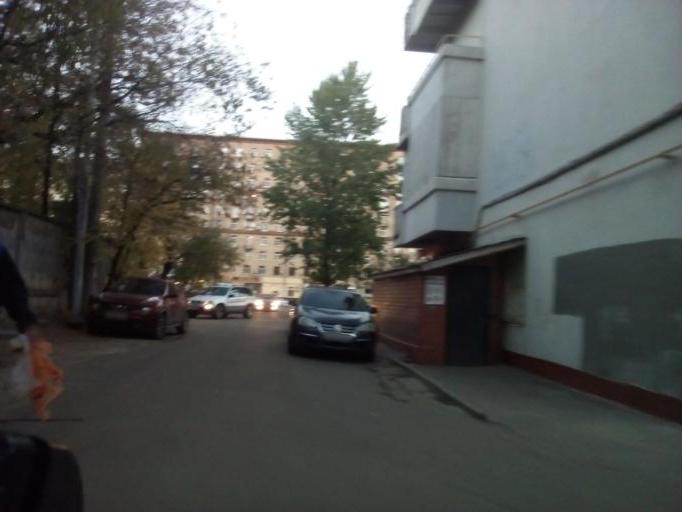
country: RU
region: Moscow
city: Sokol
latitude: 55.8071
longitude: 37.4996
